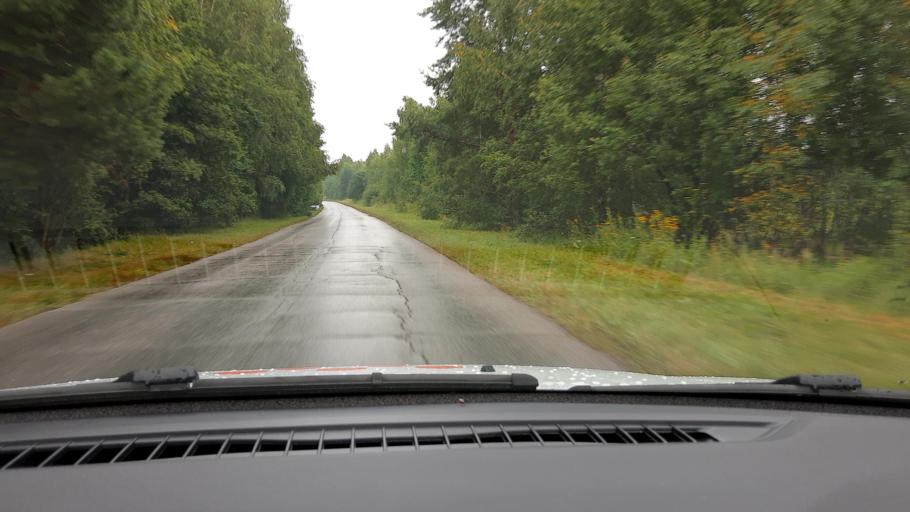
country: RU
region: Nizjnij Novgorod
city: Dal'neye Konstantinovo
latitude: 55.9504
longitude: 43.9649
